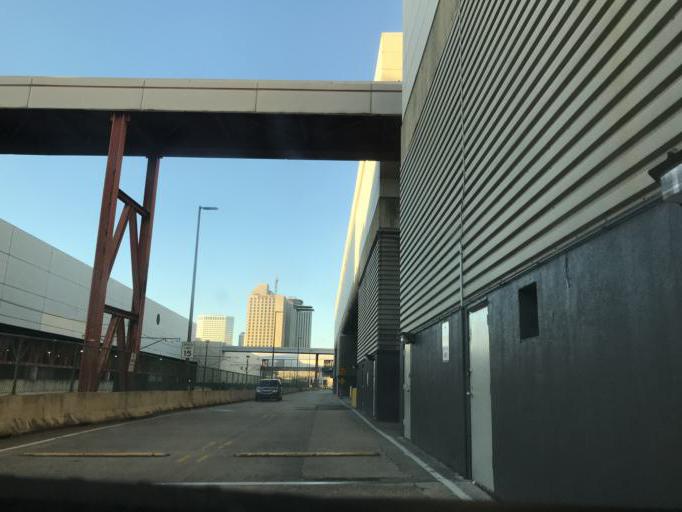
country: US
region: Louisiana
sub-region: Orleans Parish
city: New Orleans
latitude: 29.9416
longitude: -90.0621
